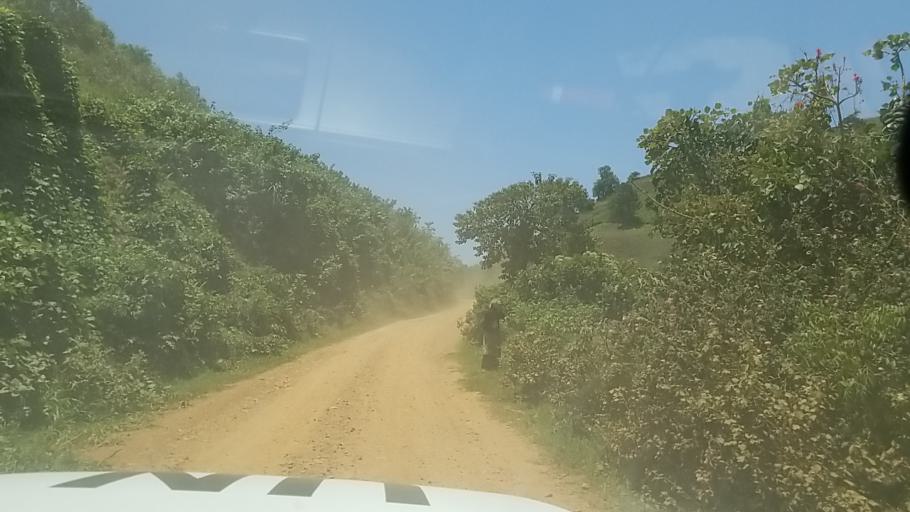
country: CD
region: Nord Kivu
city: Sake
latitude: -1.8171
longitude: 29.0059
